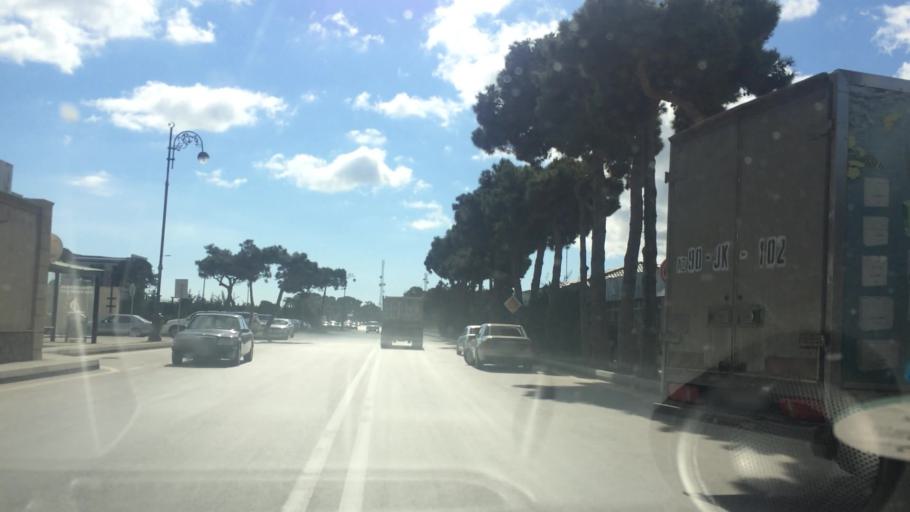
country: AZ
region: Baki
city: Pirallahi
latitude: 40.4683
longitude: 50.3262
